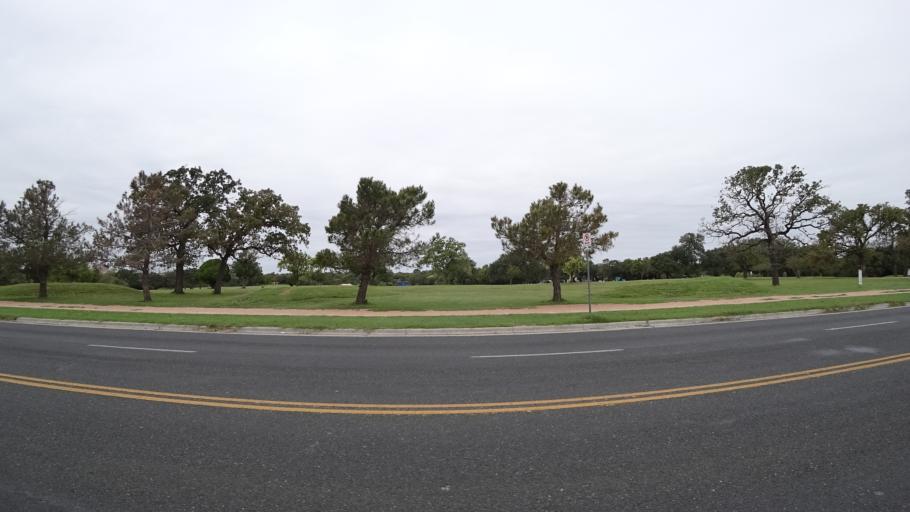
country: US
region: Texas
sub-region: Travis County
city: Austin
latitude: 30.2982
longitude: -97.7227
